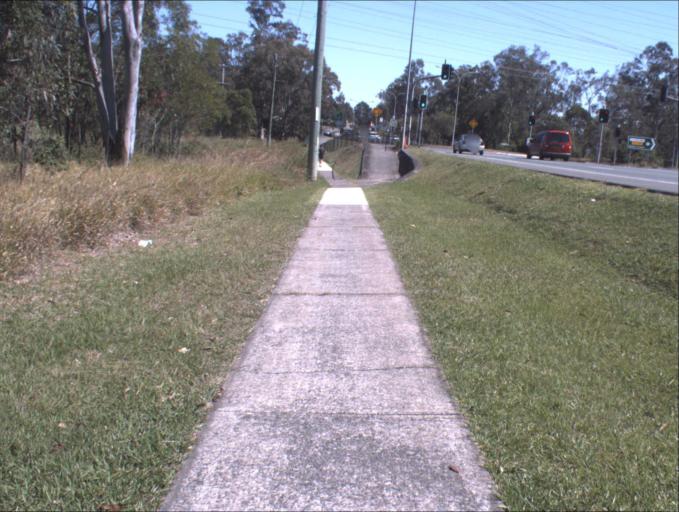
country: AU
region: Queensland
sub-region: Logan
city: Waterford West
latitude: -27.6668
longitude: 153.1206
